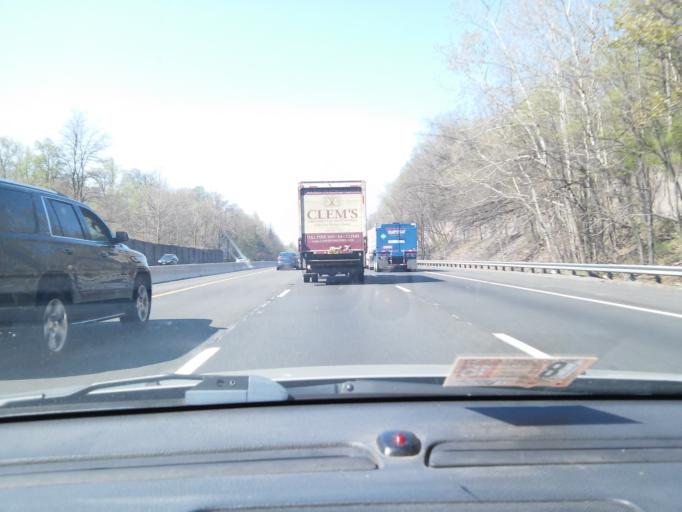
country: US
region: New Jersey
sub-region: Union County
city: New Providence
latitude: 40.6931
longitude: -74.3755
